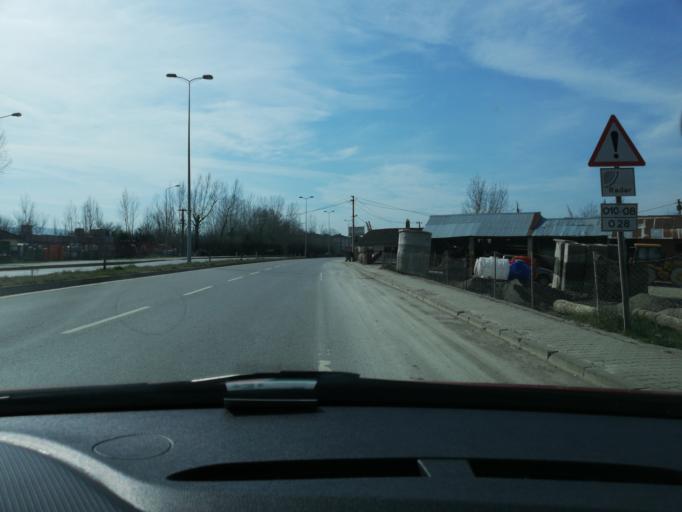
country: TR
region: Bartin
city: Bartin
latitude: 41.6410
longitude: 32.3551
